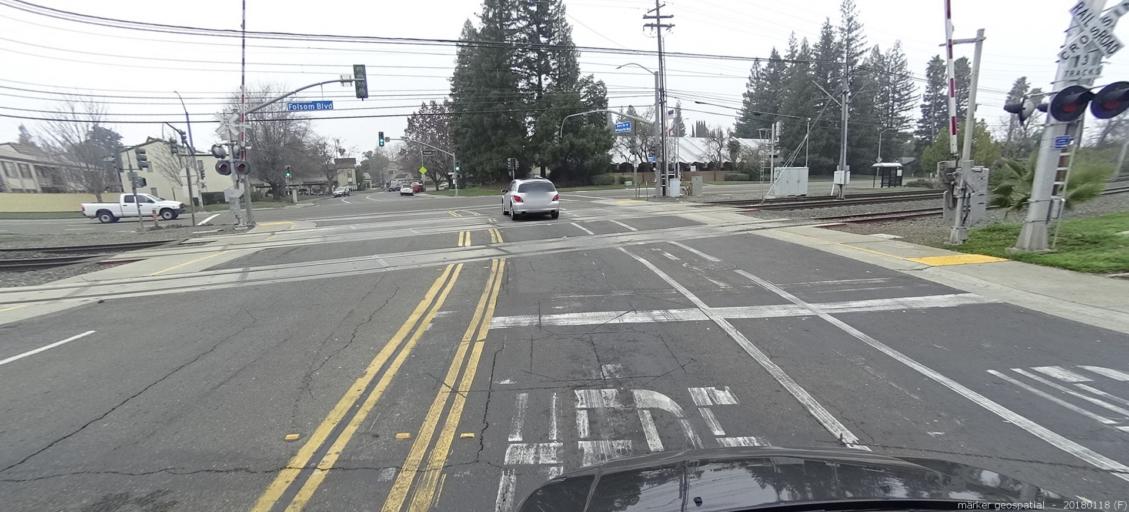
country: US
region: California
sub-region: Sacramento County
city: La Riviera
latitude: 38.5756
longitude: -121.3293
